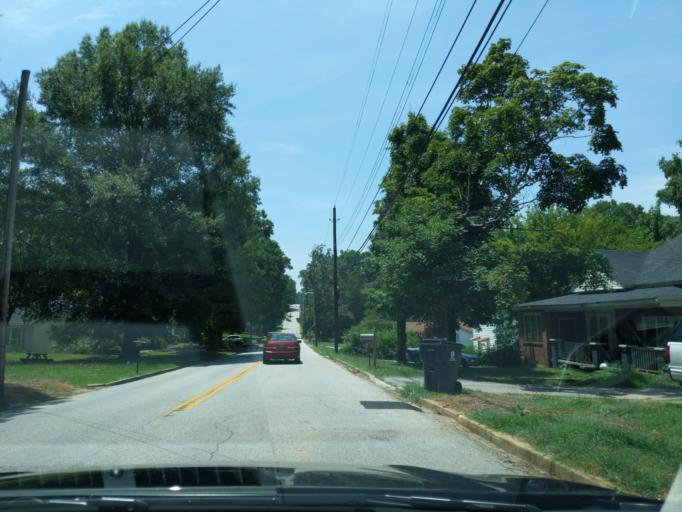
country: US
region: South Carolina
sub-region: Laurens County
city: Laurens
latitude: 34.4938
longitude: -82.0193
